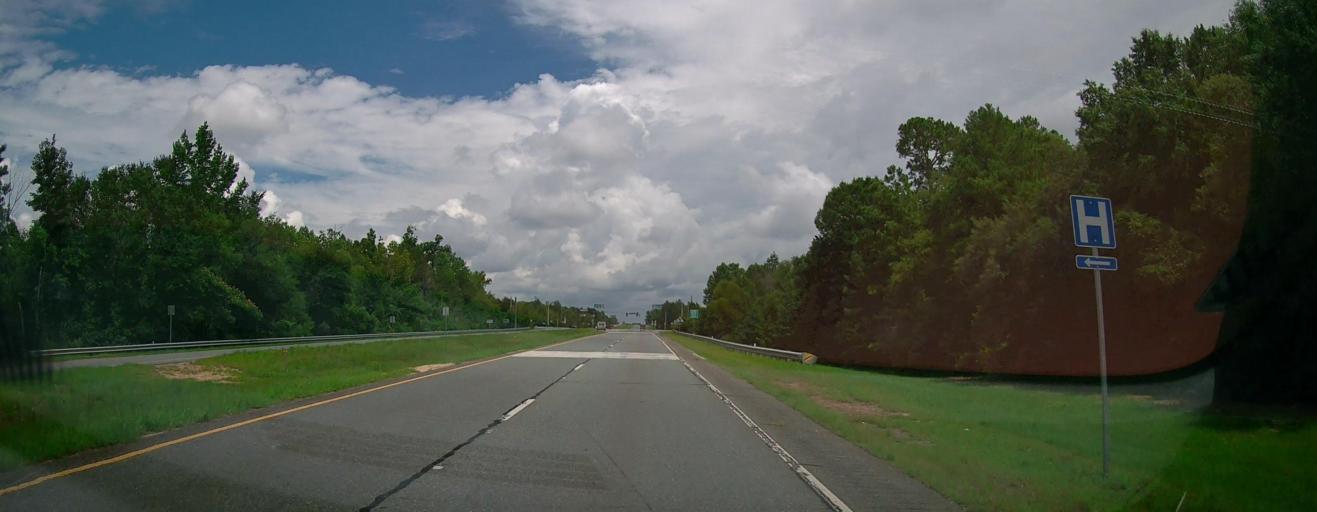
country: US
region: Georgia
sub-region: Dodge County
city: Eastman
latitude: 32.1782
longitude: -83.1847
